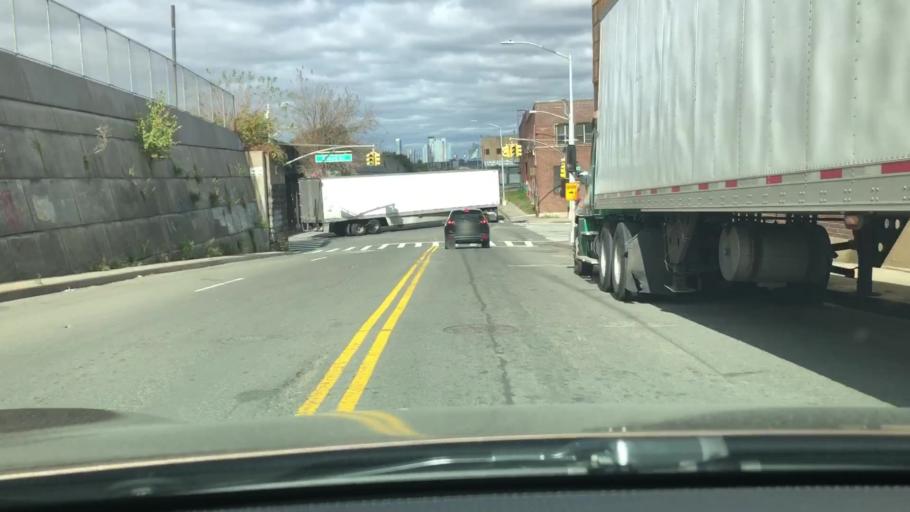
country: US
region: New York
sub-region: Queens County
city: Long Island City
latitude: 40.7192
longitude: -73.9110
